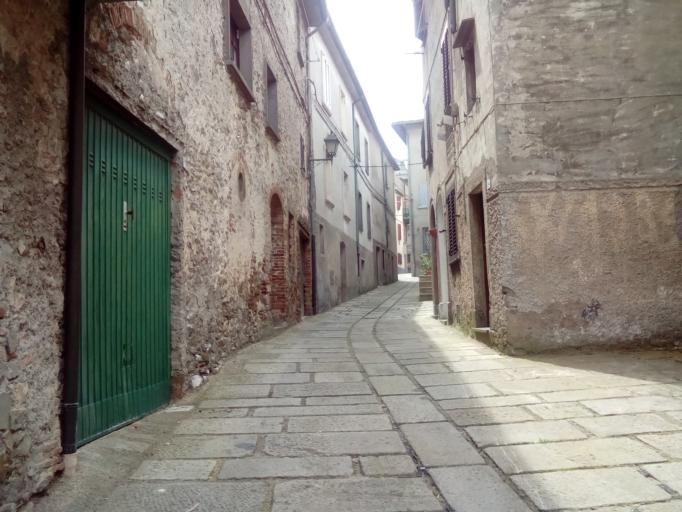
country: IT
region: Tuscany
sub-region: Provincia di Grosseto
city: Castell'Azzara
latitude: 42.7715
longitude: 11.6991
